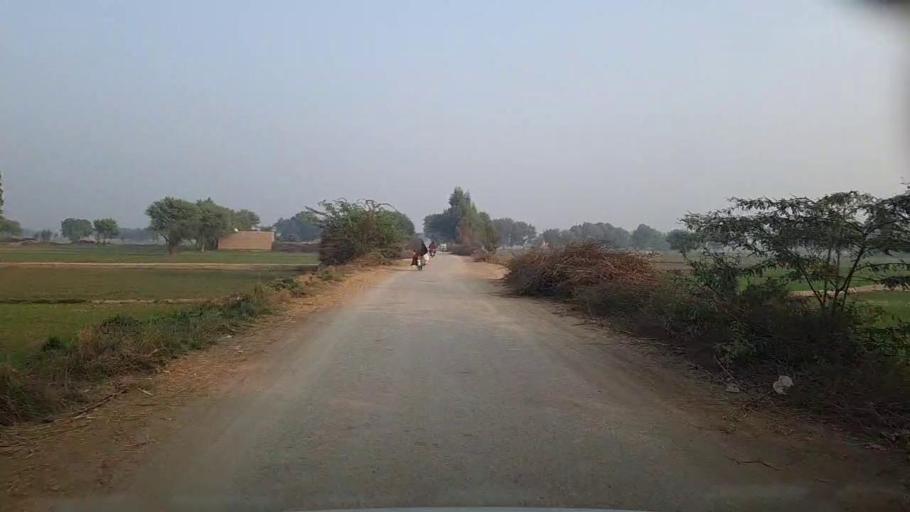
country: PK
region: Sindh
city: Bozdar
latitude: 27.0820
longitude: 68.5690
